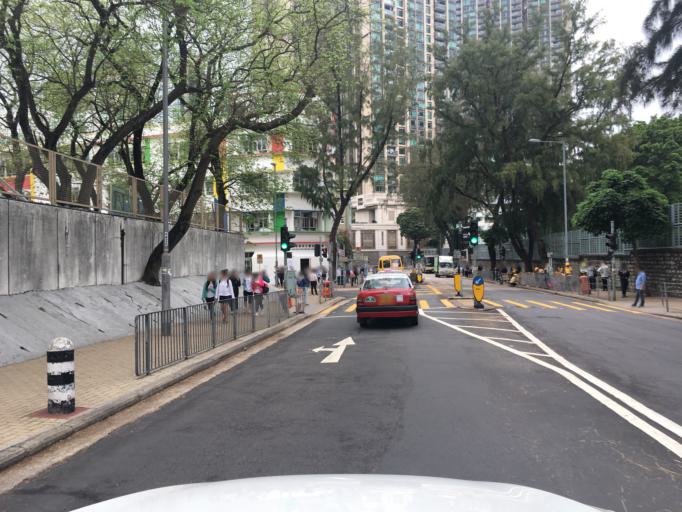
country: HK
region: Kowloon City
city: Kowloon
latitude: 22.3213
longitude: 114.1850
